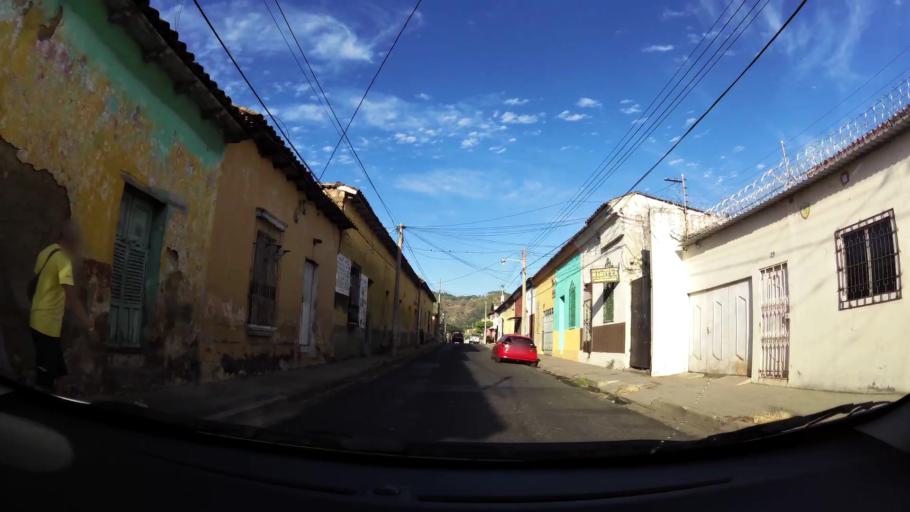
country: SV
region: Santa Ana
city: Santa Ana
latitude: 13.9967
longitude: -89.5539
